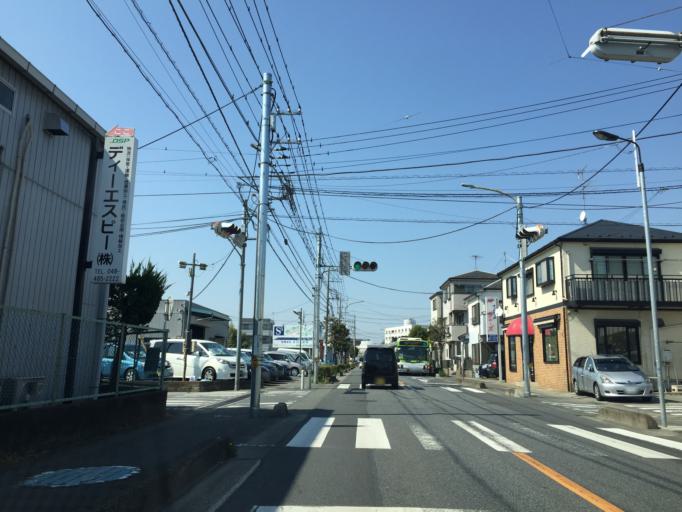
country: JP
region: Saitama
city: Shiki
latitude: 35.8479
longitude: 139.5885
